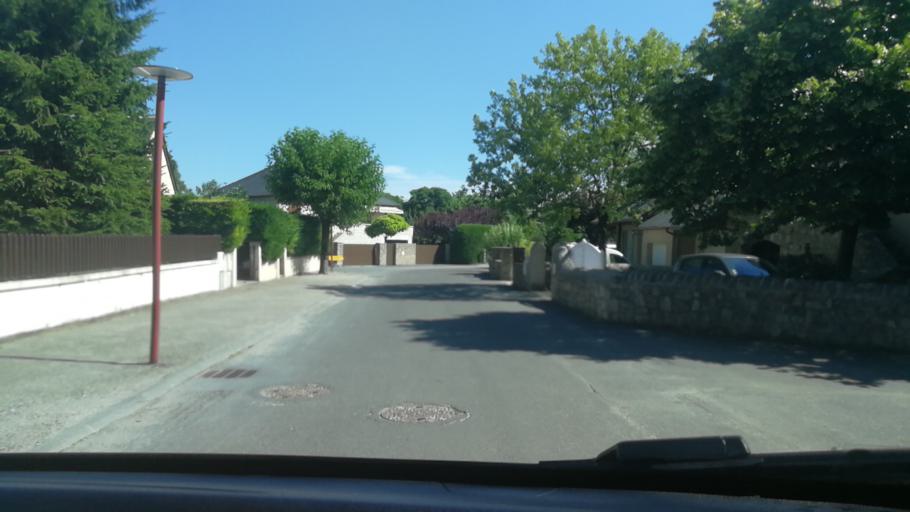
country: FR
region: Midi-Pyrenees
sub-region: Departement de l'Aveyron
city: Sebazac-Concoures
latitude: 44.4004
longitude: 2.5973
